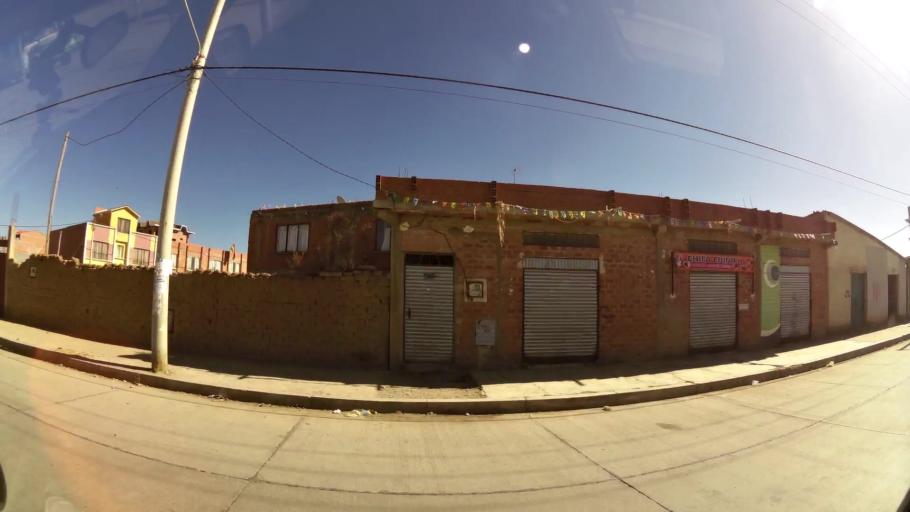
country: BO
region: La Paz
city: La Paz
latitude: -16.5312
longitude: -68.2353
